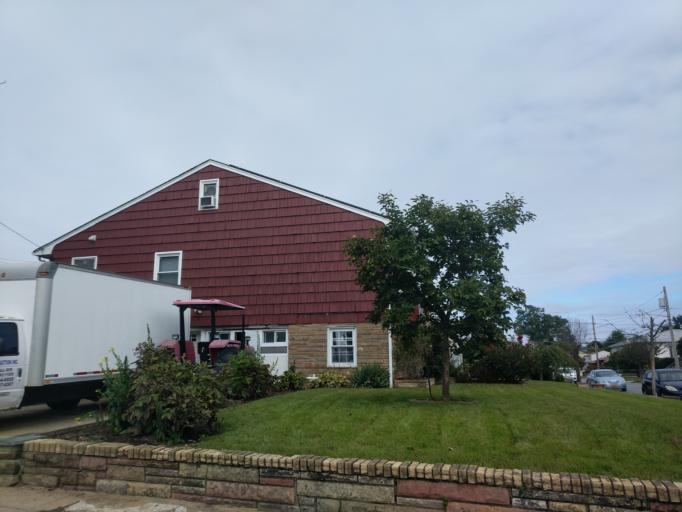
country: US
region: New York
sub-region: Nassau County
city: Inwood
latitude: 40.6225
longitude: -73.7377
